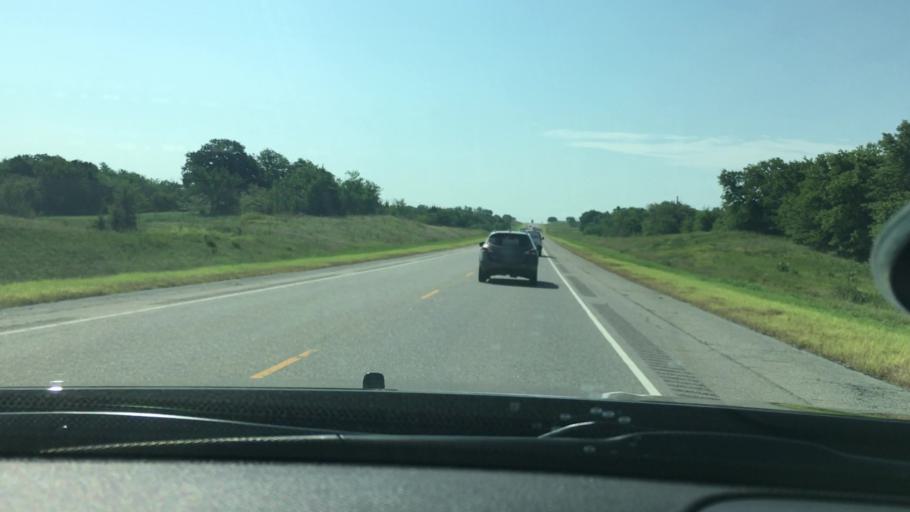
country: US
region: Oklahoma
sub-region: Coal County
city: Coalgate
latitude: 34.6258
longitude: -96.4617
